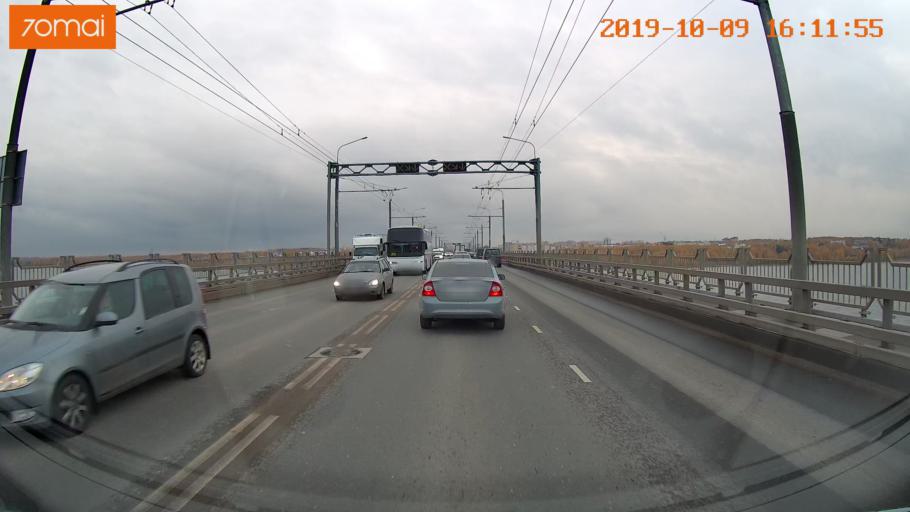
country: RU
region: Kostroma
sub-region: Kostromskoy Rayon
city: Kostroma
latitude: 57.7552
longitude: 40.9424
